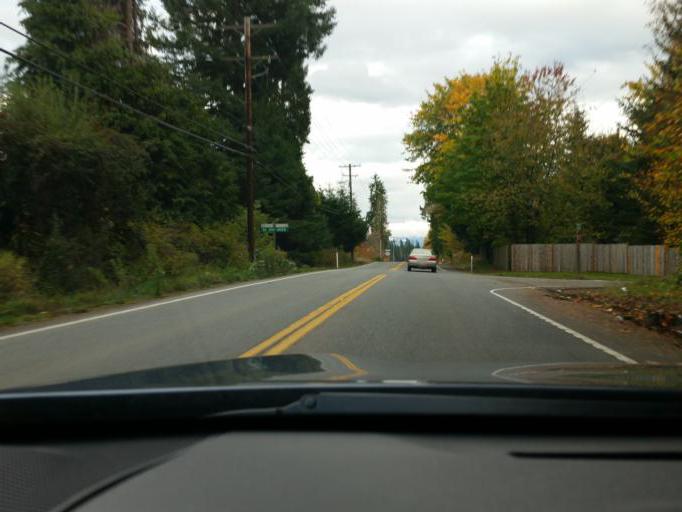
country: US
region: Washington
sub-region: Snohomish County
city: Maltby
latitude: 47.8051
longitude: -122.1229
